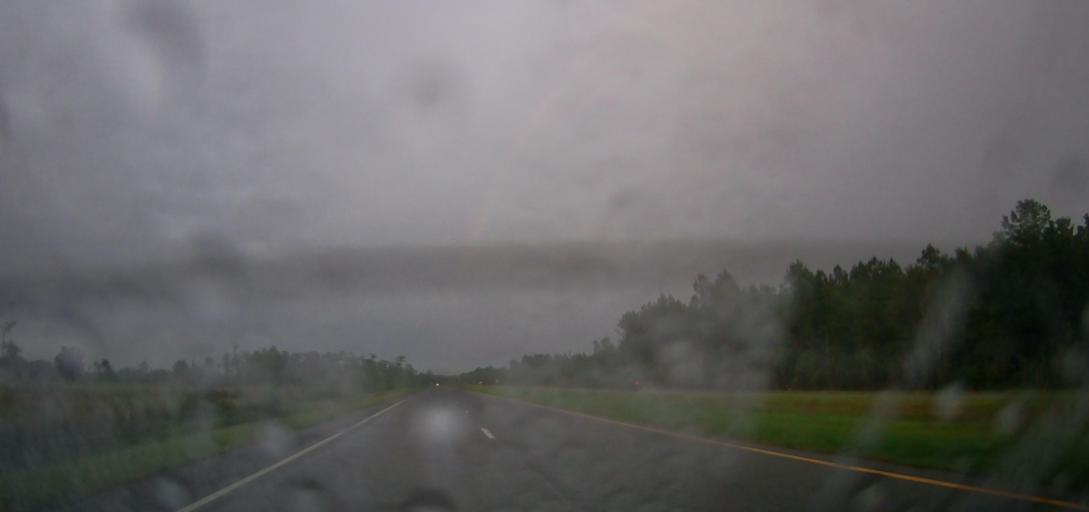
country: US
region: Georgia
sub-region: Clinch County
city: Homerville
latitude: 30.9797
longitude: -82.8963
